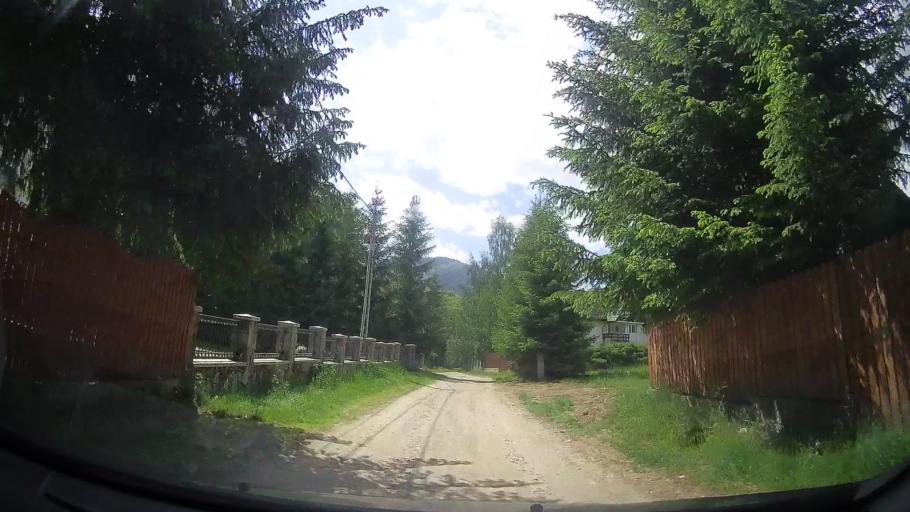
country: RO
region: Brasov
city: Crivina
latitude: 45.4596
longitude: 25.9492
